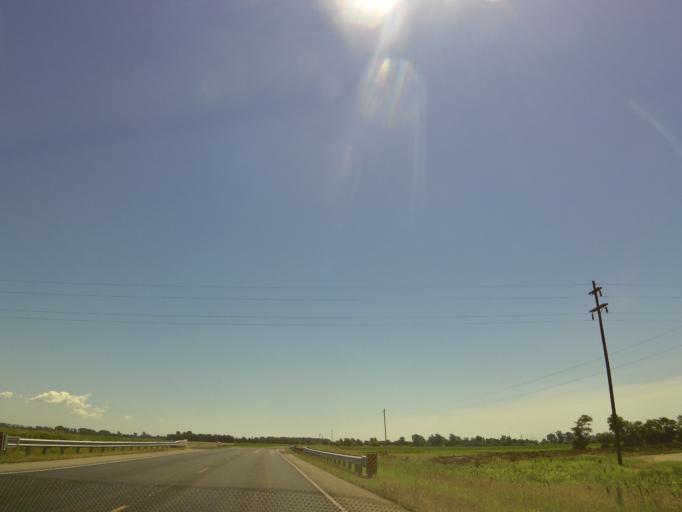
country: US
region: Missouri
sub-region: New Madrid County
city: Lilbourn
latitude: 36.5547
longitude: -89.6846
